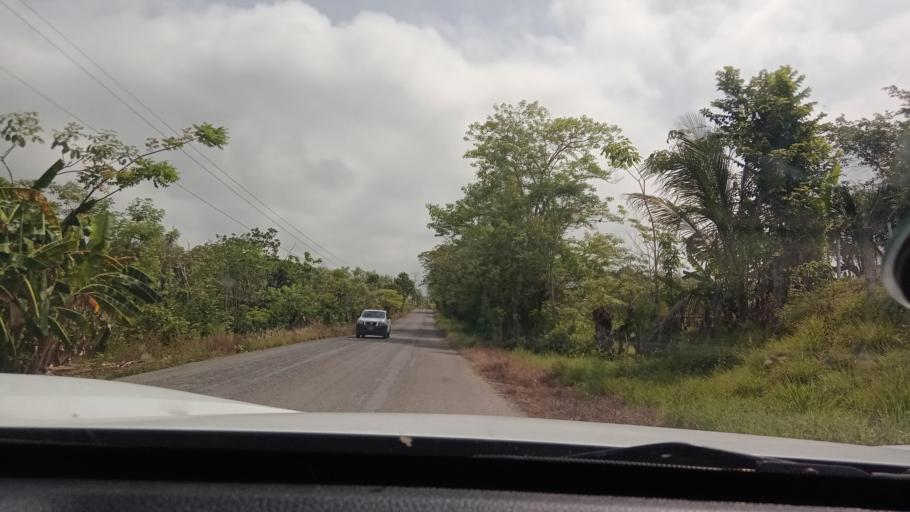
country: MX
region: Tabasco
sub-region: Huimanguillo
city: Francisco Rueda
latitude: 17.5712
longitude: -94.1093
